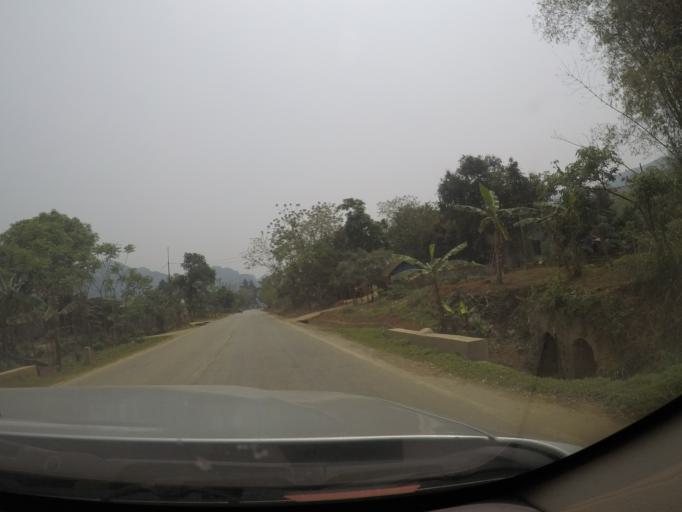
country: VN
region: Thanh Hoa
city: Thi Tran Ngoc Lac
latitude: 20.0748
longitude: 105.3793
